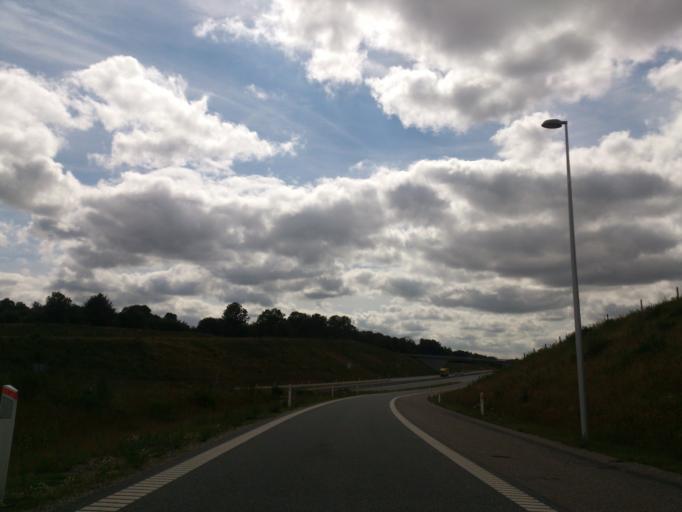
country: DK
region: South Denmark
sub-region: Aabenraa Kommune
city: Aabenraa
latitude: 54.9453
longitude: 9.4501
